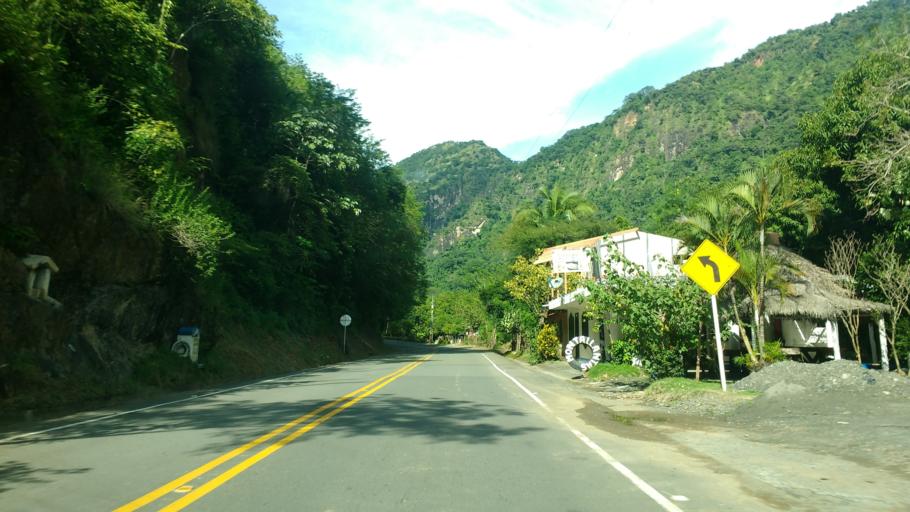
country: CO
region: Antioquia
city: Concordia
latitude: 6.0636
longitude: -75.8629
